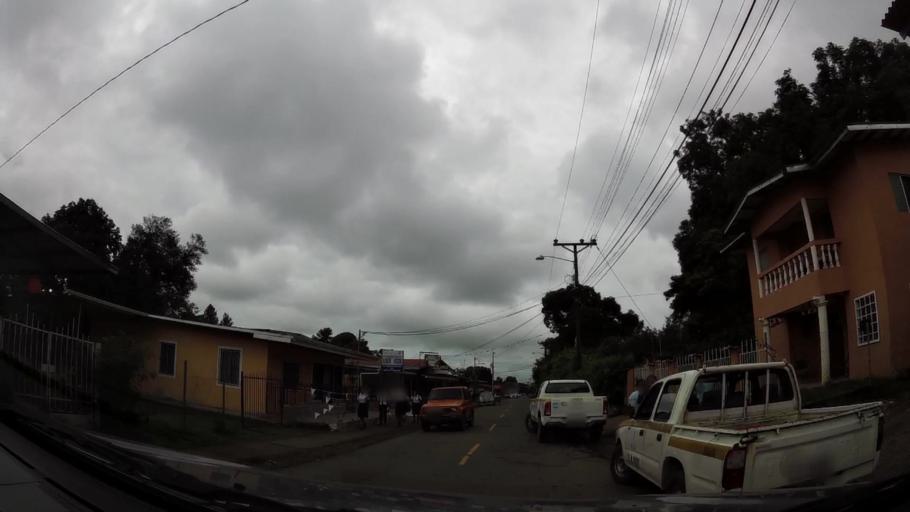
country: PA
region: Chiriqui
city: Dolega District
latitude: 8.5646
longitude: -82.4153
